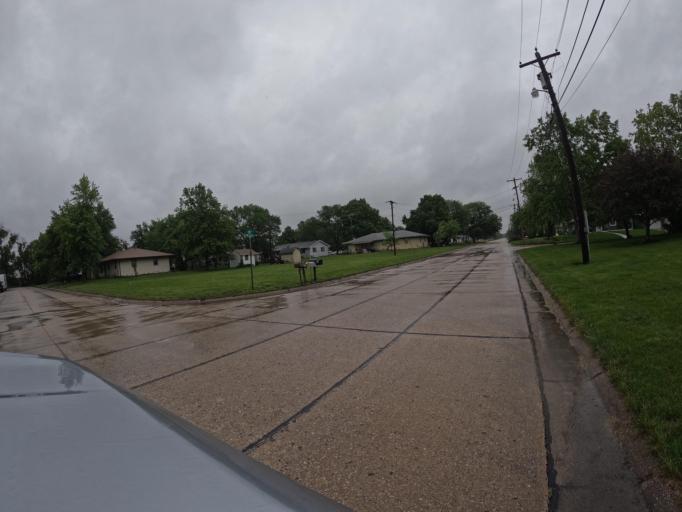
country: US
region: Nebraska
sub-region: Saline County
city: Wilber
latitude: 40.3966
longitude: -96.9313
